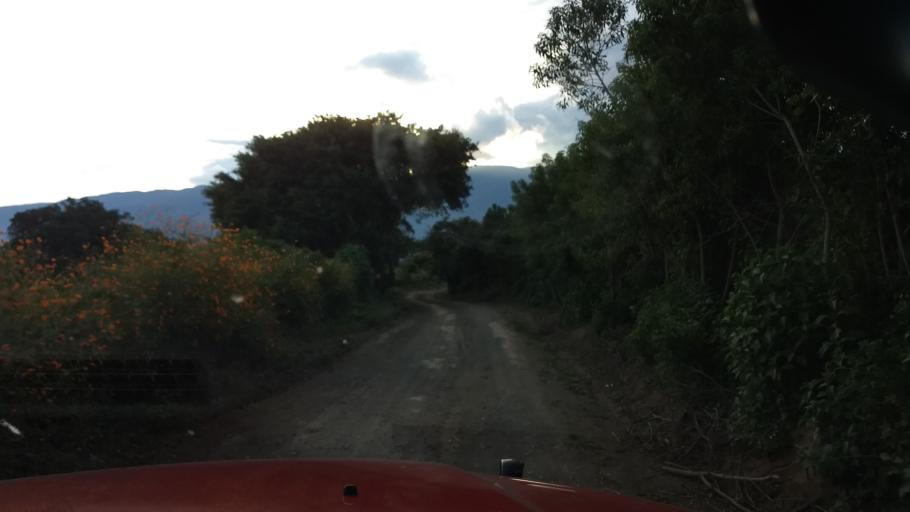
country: MX
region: Colima
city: Suchitlan
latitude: 19.4959
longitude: -103.7758
